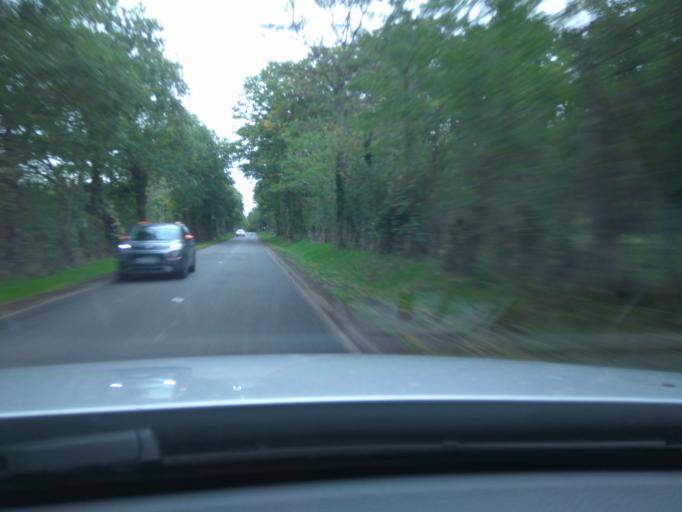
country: FR
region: Centre
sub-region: Departement du Cher
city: Saint-Satur
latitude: 47.3495
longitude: 2.8855
